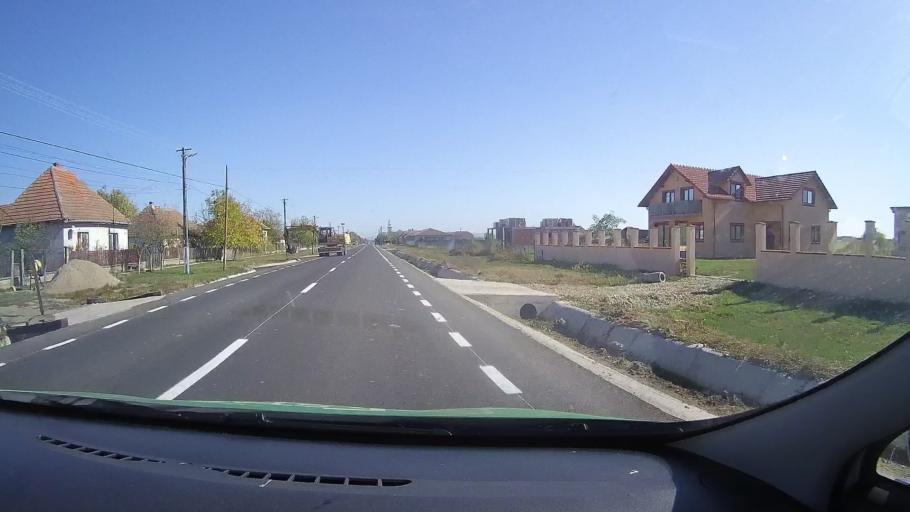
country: RO
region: Satu Mare
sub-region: Oras Ardud
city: Madaras
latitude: 47.6856
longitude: 22.8504
